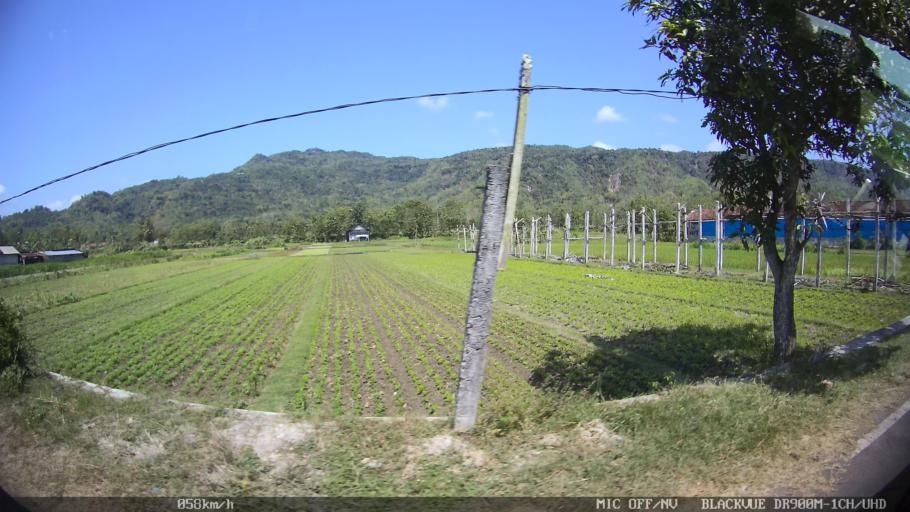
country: ID
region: Daerah Istimewa Yogyakarta
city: Pundong
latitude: -7.9690
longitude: 110.3522
